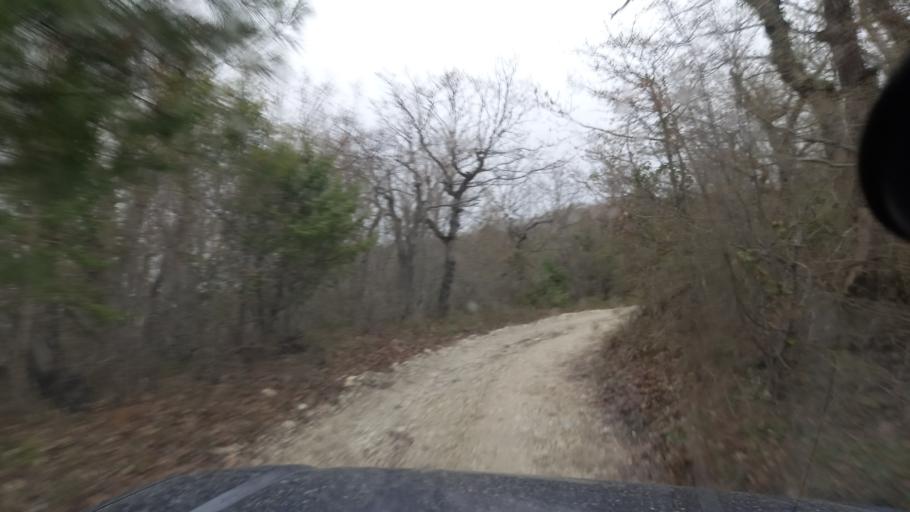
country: RU
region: Krasnodarskiy
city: Dzhubga
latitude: 44.3205
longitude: 38.6750
